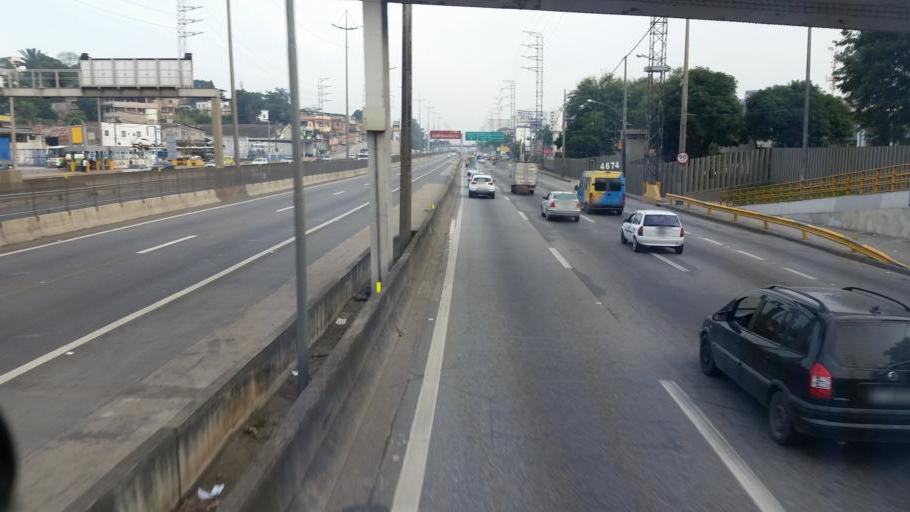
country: BR
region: Rio de Janeiro
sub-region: Sao Joao De Meriti
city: Sao Joao de Meriti
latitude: -22.7978
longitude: -43.3575
